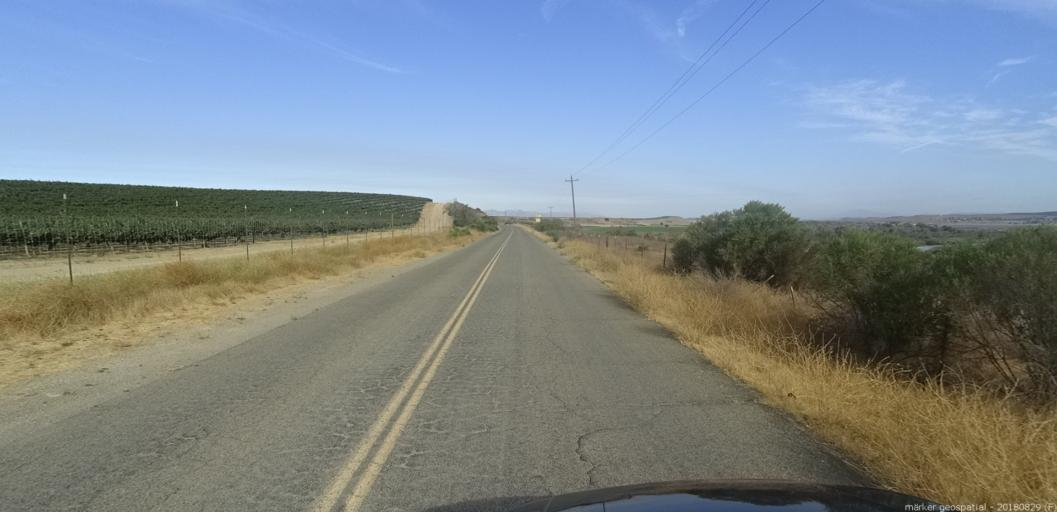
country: US
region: California
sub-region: Monterey County
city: King City
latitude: 36.0935
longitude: -121.0125
